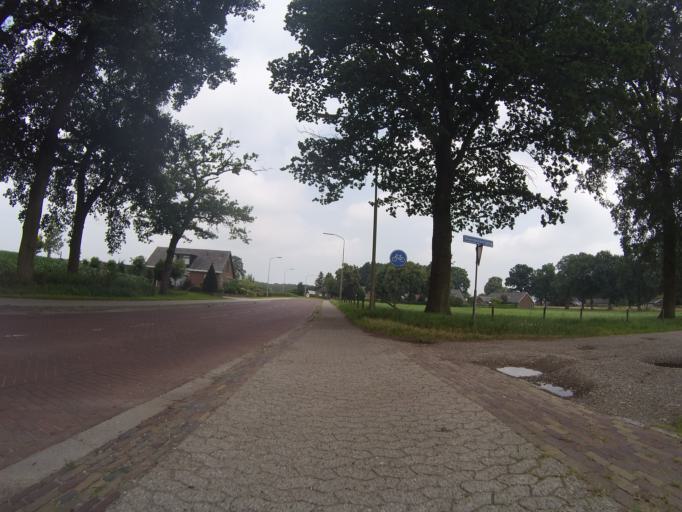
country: NL
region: Drenthe
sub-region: Gemeente Emmen
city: Emmen
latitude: 52.8139
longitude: 6.9090
